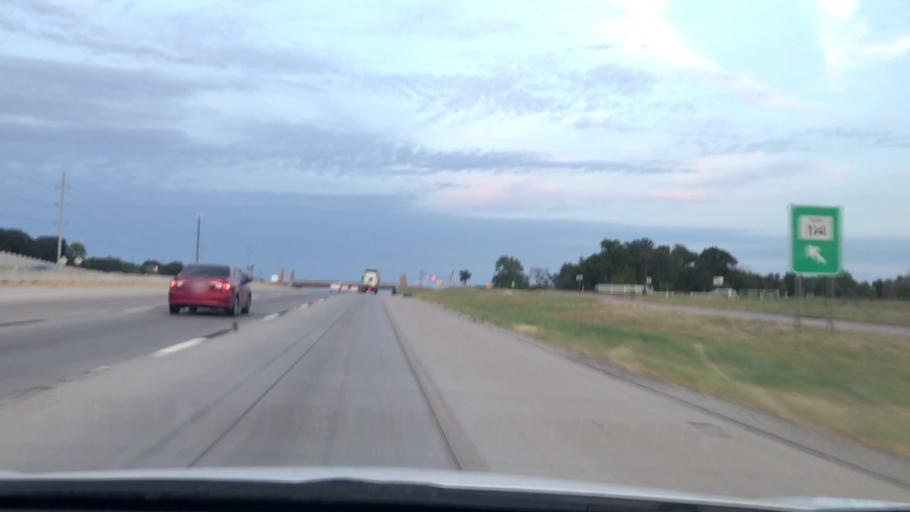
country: US
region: Texas
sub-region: Denton County
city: Trophy Club
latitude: 32.9904
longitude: -97.1862
